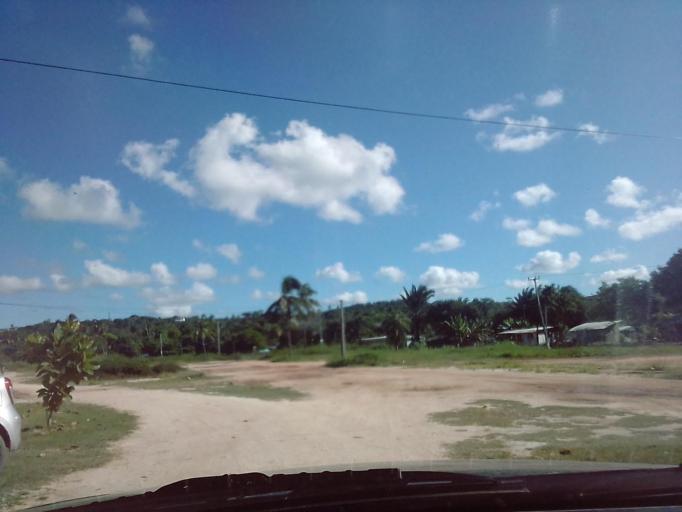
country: BR
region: Pernambuco
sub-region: Igarassu
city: Igarassu
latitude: -7.8377
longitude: -34.8455
